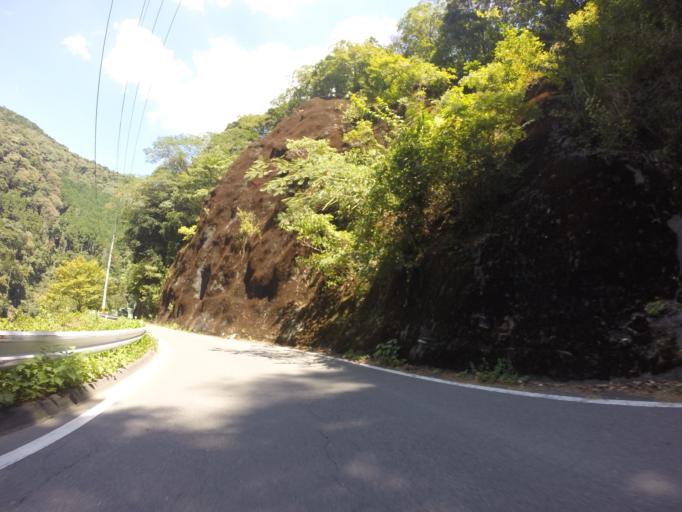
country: JP
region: Shizuoka
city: Shizuoka-shi
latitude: 35.0587
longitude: 138.2434
